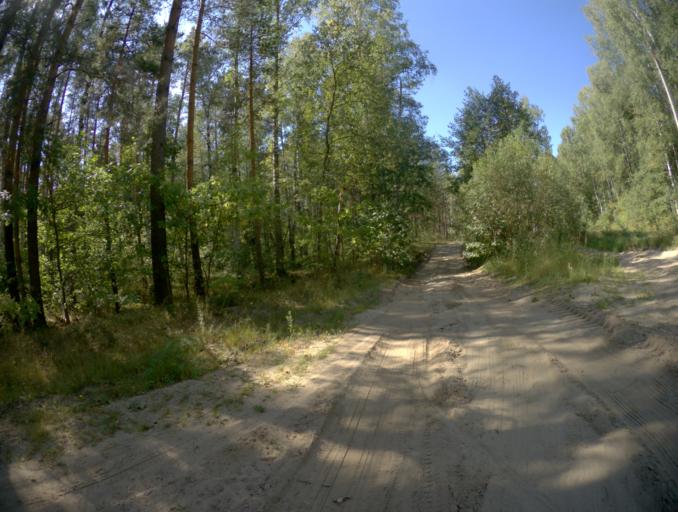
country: RU
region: Vladimir
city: Petushki
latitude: 55.8648
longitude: 39.3789
